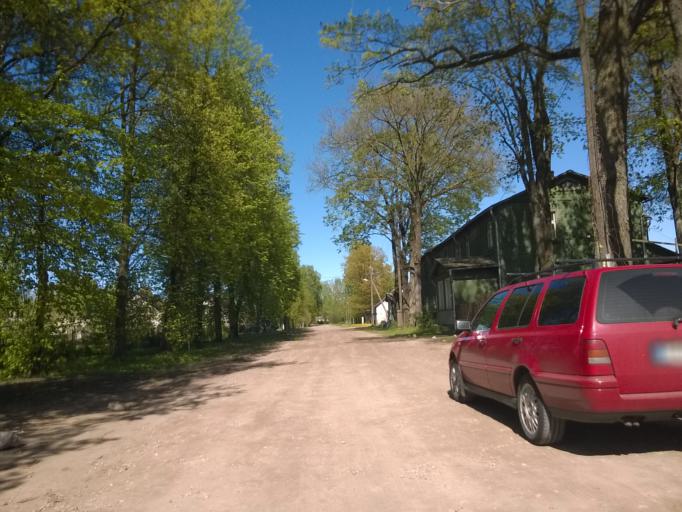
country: LV
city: Tireli
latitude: 56.9498
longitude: 23.6203
